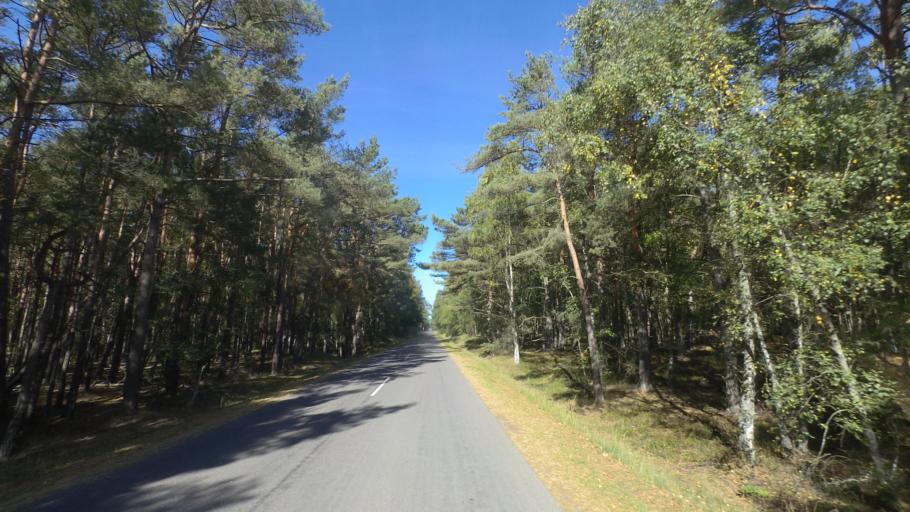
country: DK
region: Capital Region
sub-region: Bornholm Kommune
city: Nexo
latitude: 54.9966
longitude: 15.0768
